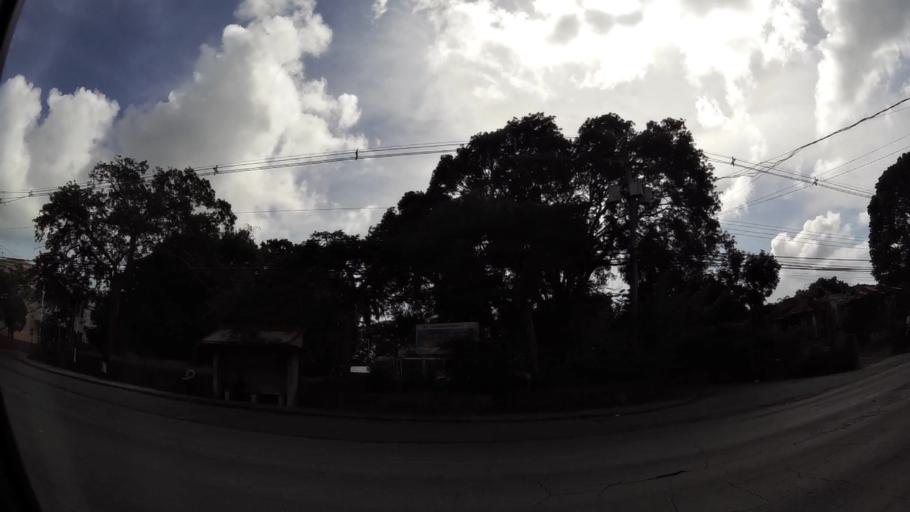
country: BB
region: Saint Michael
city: Bridgetown
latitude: 13.0930
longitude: -59.6041
